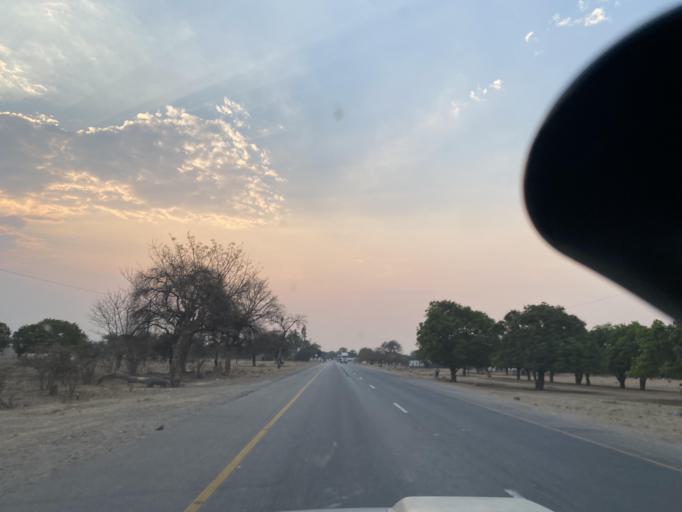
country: ZM
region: Lusaka
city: Kafue
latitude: -15.8746
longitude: 28.2890
